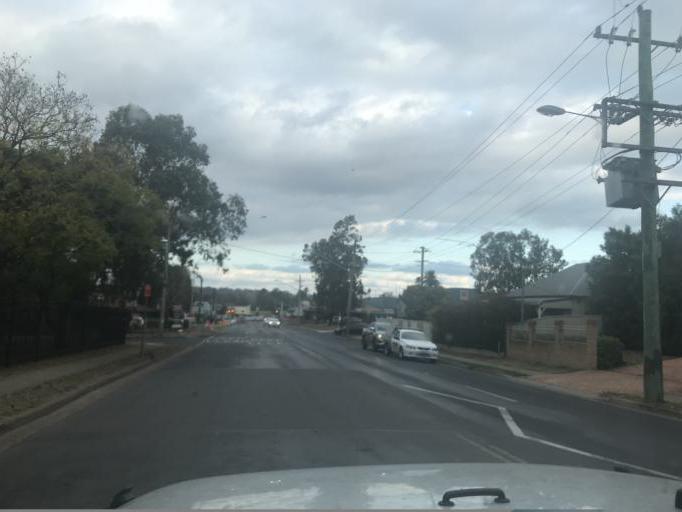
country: AU
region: New South Wales
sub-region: Hawkesbury
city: Richmond
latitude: -33.5811
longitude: 150.7178
